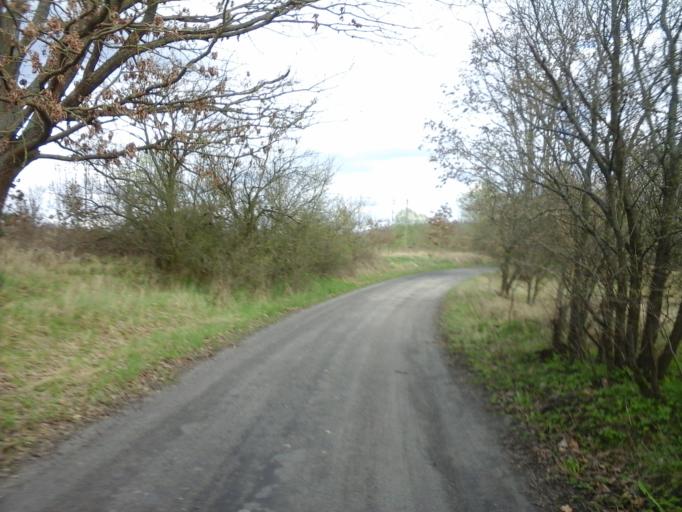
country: PL
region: West Pomeranian Voivodeship
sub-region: Powiat choszczenski
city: Krzecin
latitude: 53.0707
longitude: 15.5784
